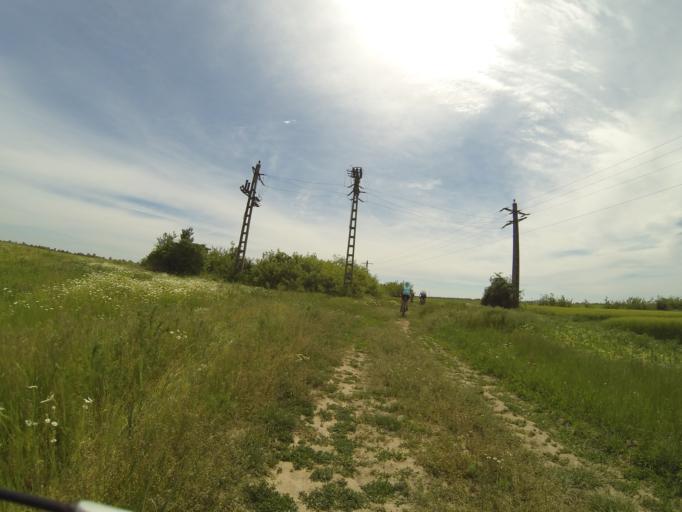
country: RO
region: Dolj
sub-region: Comuna Leu
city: Leu
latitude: 44.2040
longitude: 23.9667
